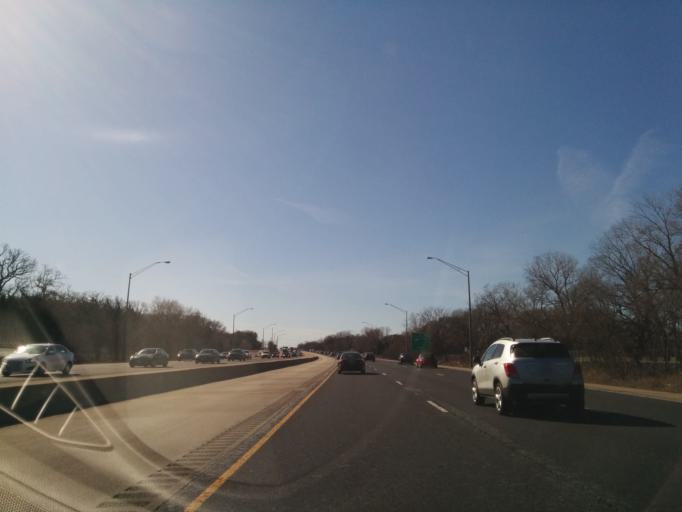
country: US
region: Illinois
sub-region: DuPage County
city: Darien
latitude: 41.7267
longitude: -87.9873
